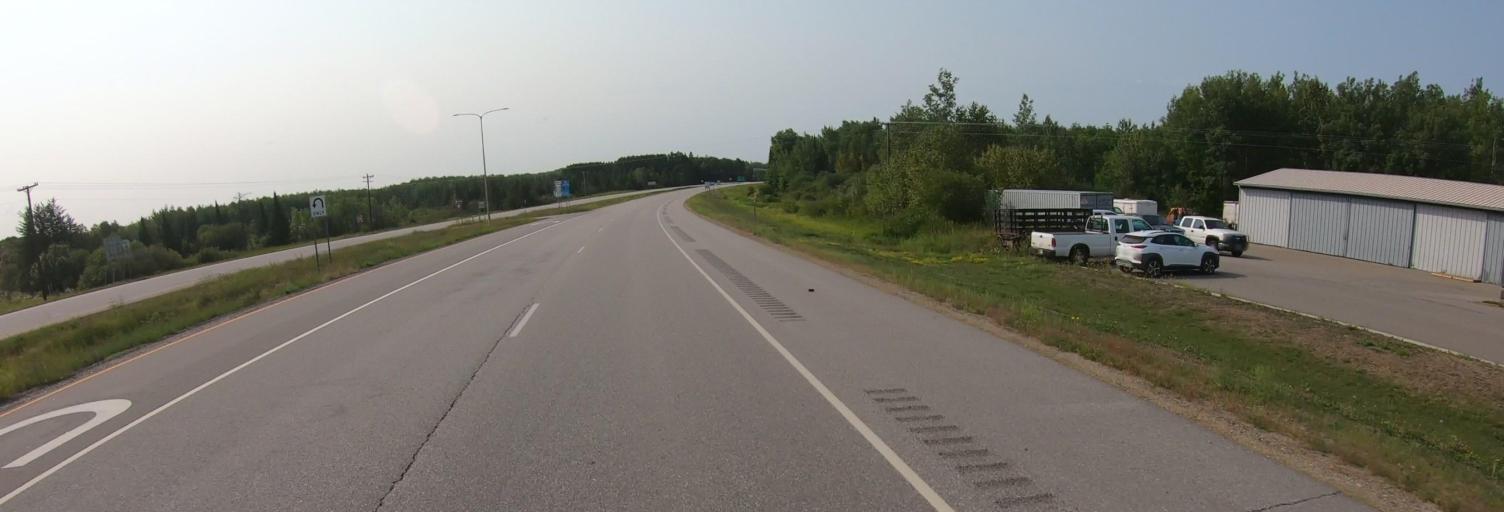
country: US
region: Minnesota
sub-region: Saint Louis County
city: Mountain Iron
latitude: 47.7791
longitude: -92.6561
